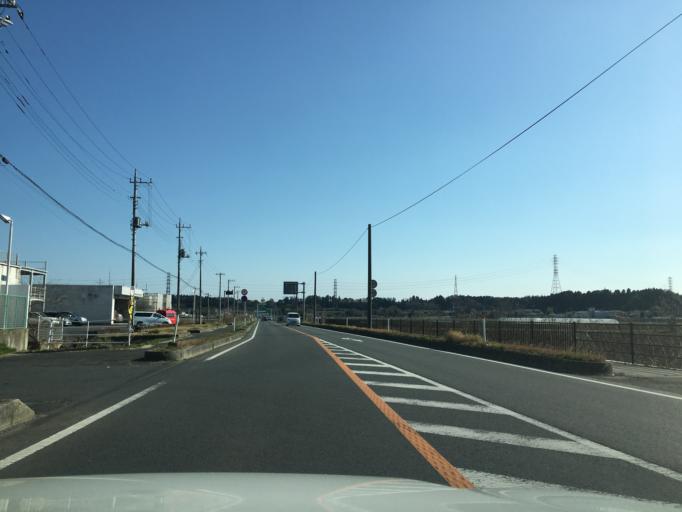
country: JP
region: Ibaraki
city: Mito-shi
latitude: 36.4234
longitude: 140.4224
